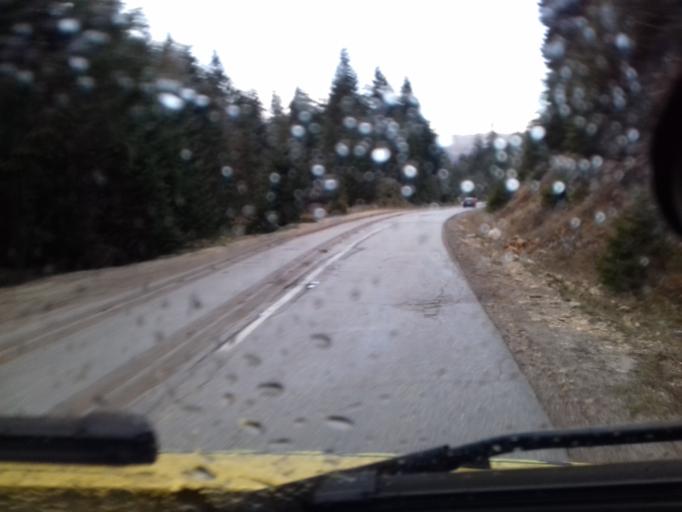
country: BA
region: Federation of Bosnia and Herzegovina
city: Turbe
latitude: 44.3126
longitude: 17.4964
